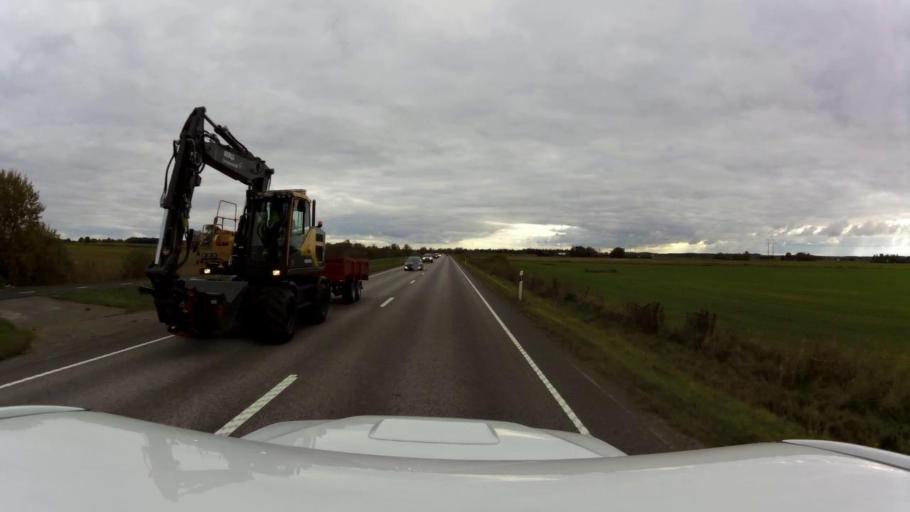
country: SE
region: OEstergoetland
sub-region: Linkopings Kommun
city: Berg
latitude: 58.4590
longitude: 15.5449
